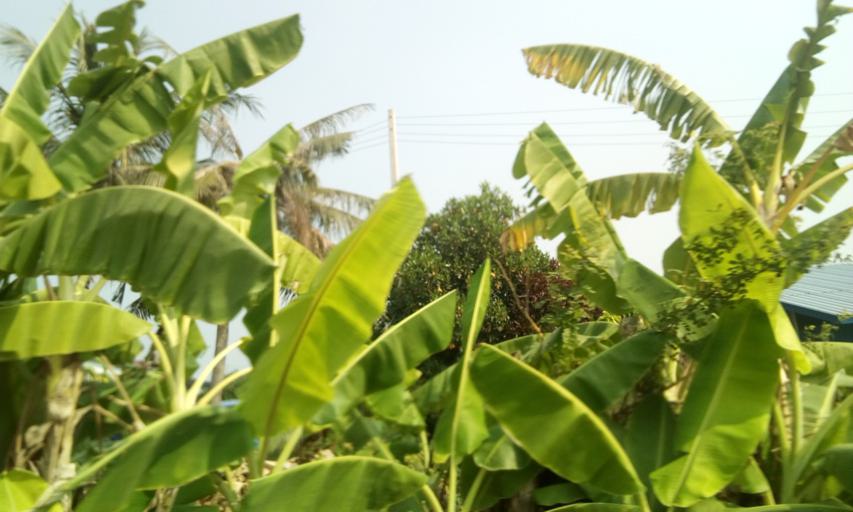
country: TH
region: Pathum Thani
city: Lam Luk Ka
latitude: 13.9506
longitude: 100.7248
